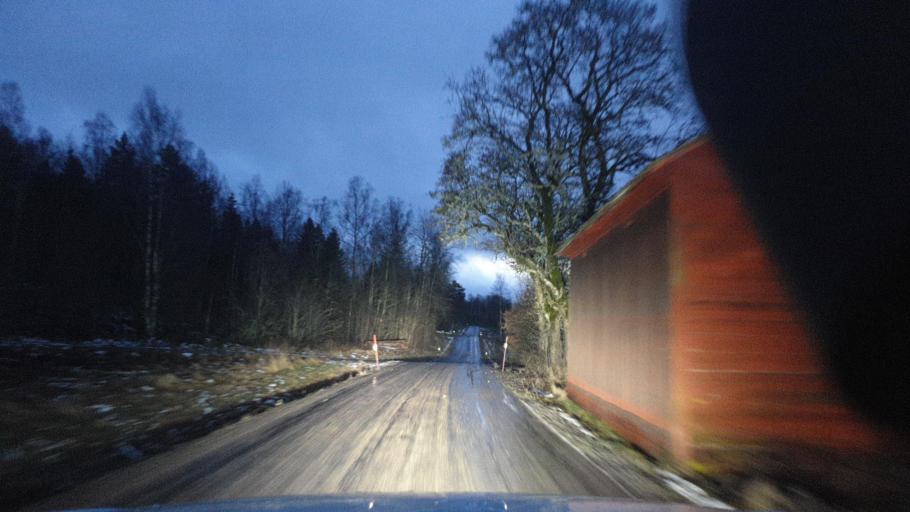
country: SE
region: Vaermland
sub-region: Eda Kommun
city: Amotfors
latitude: 59.7708
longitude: 12.4437
